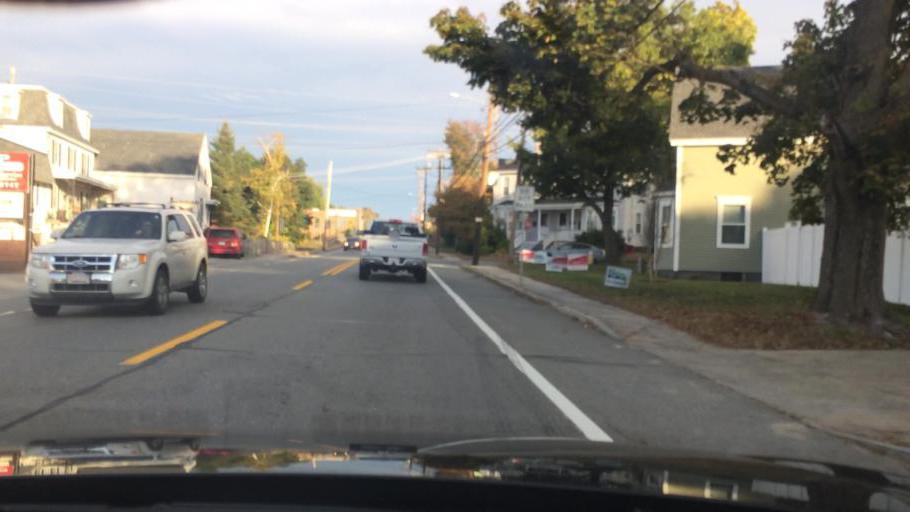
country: US
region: Massachusetts
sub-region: Middlesex County
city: Chelmsford
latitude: 42.6345
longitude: -71.3777
